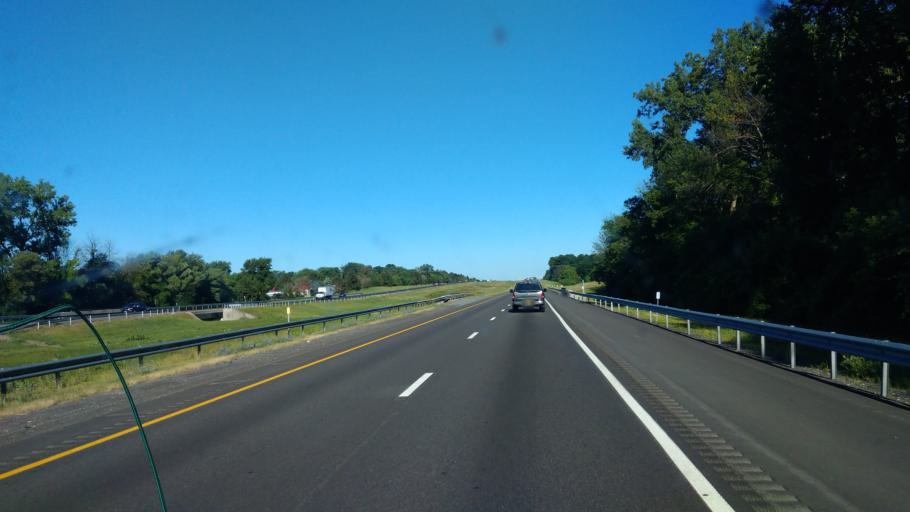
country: US
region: New York
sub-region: Ontario County
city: Clifton Springs
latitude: 42.9735
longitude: -77.1564
